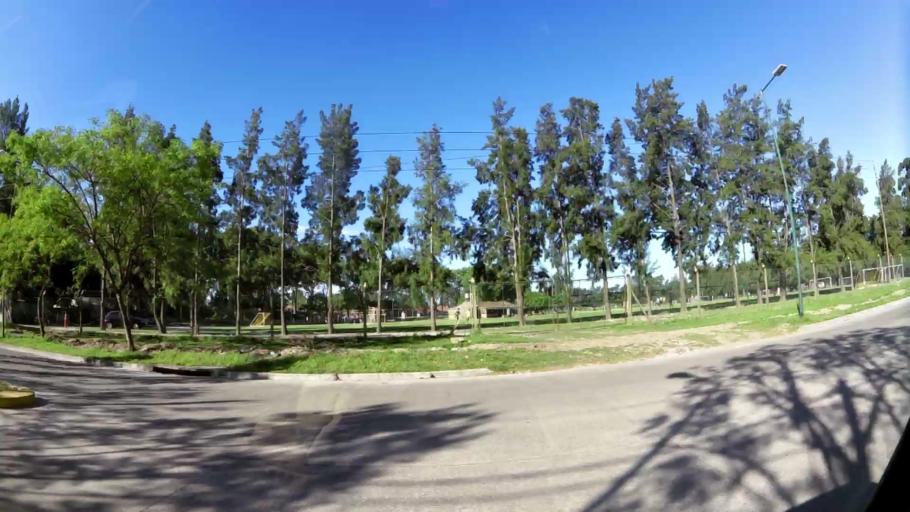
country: AR
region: Buenos Aires
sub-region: Partido de San Isidro
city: San Isidro
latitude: -34.4645
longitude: -58.5037
